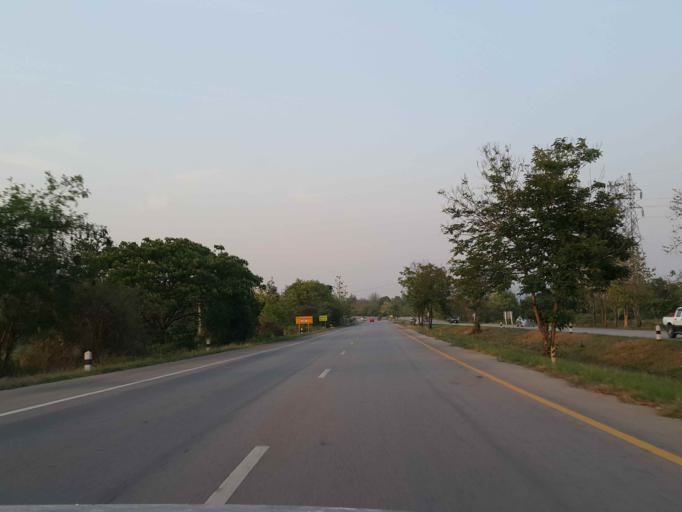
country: TH
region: Lampang
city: Sop Prap
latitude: 17.9553
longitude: 99.3517
